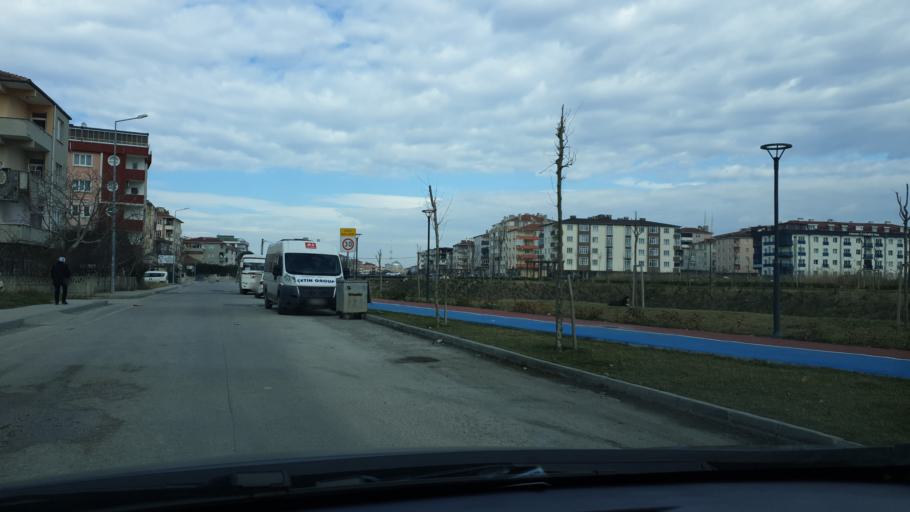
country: TR
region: Tekirdag
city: Cerkezkoey
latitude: 41.2835
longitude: 28.0036
